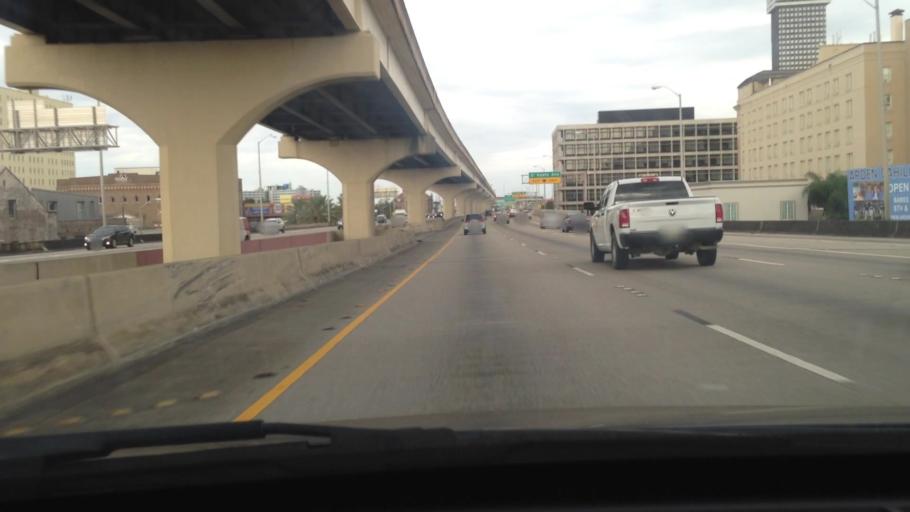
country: US
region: Louisiana
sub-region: Orleans Parish
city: New Orleans
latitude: 29.9412
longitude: -90.0714
